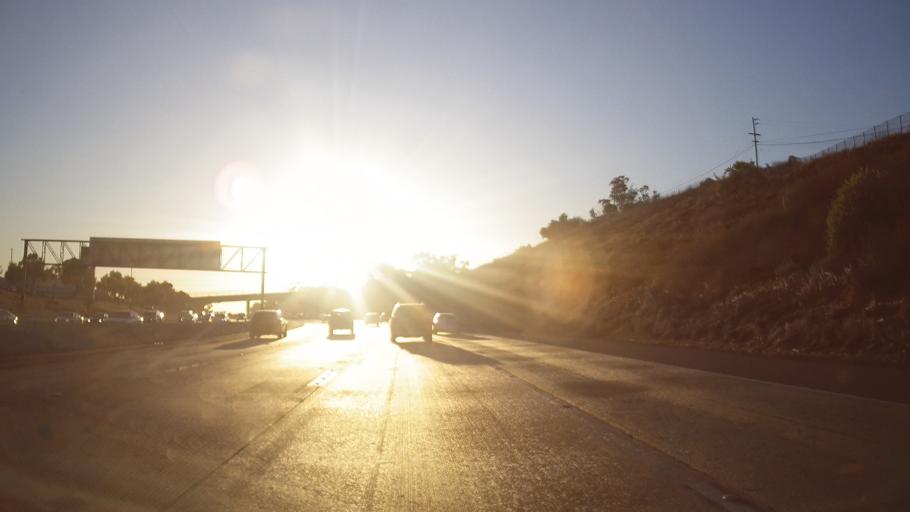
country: US
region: California
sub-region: San Diego County
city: Lemon Grove
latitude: 32.7474
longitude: -117.0272
